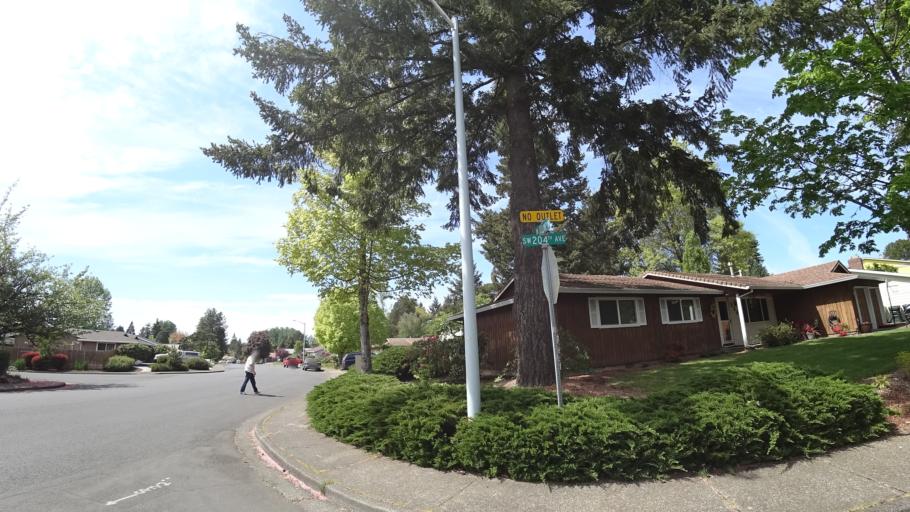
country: US
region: Oregon
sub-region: Washington County
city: Aloha
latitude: 45.4814
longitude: -122.8875
